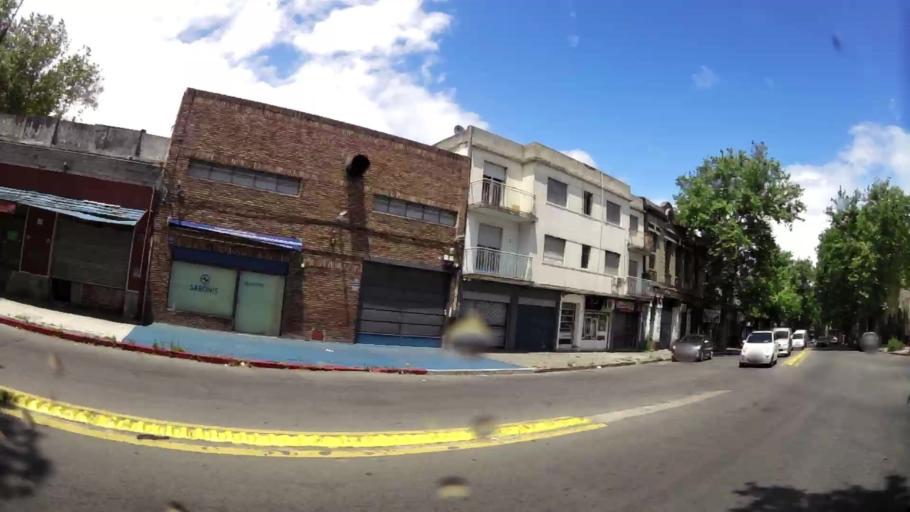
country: UY
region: Montevideo
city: Montevideo
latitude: -34.8755
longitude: -56.1852
